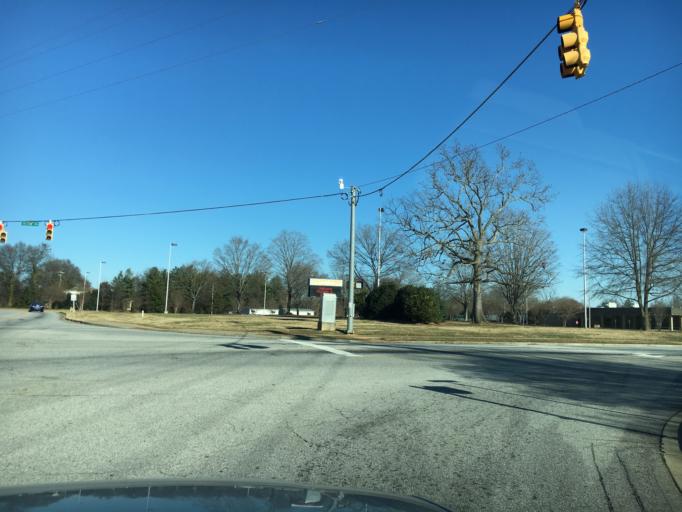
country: US
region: South Carolina
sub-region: Greenville County
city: Mauldin
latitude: 34.8115
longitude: -82.2777
